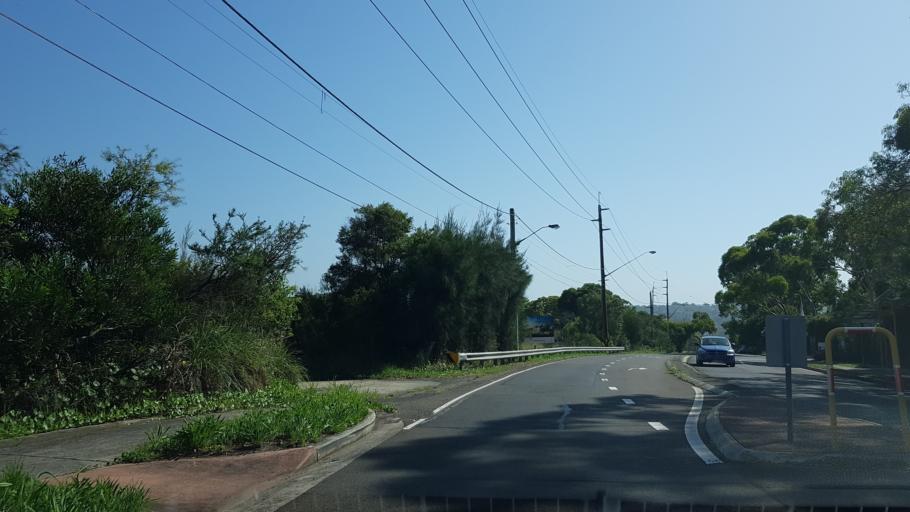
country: AU
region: New South Wales
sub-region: Warringah
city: Narraweena
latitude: -33.7447
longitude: 151.2649
